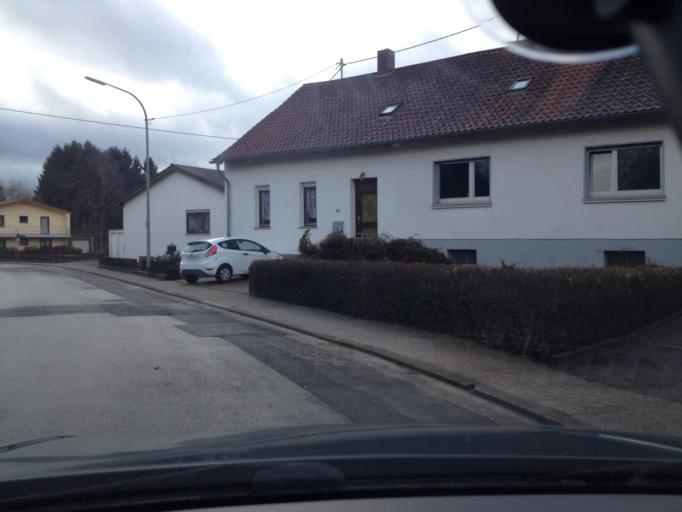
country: DE
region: Saarland
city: Sankt Wendel
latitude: 49.4972
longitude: 7.1605
